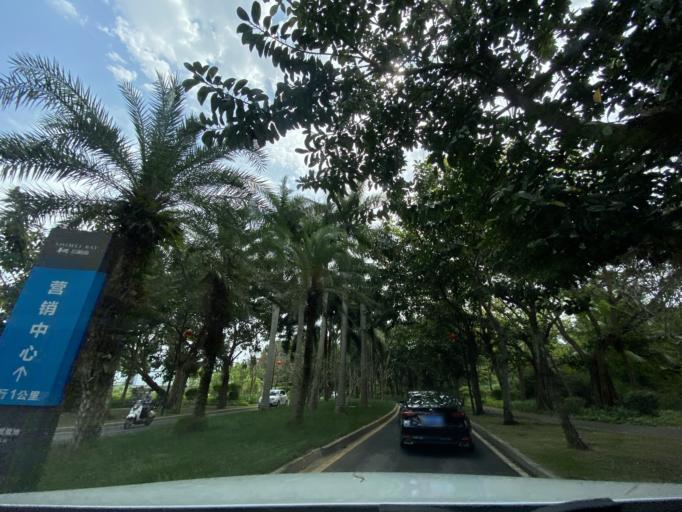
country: CN
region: Hainan
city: Liji
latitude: 18.6698
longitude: 110.2661
